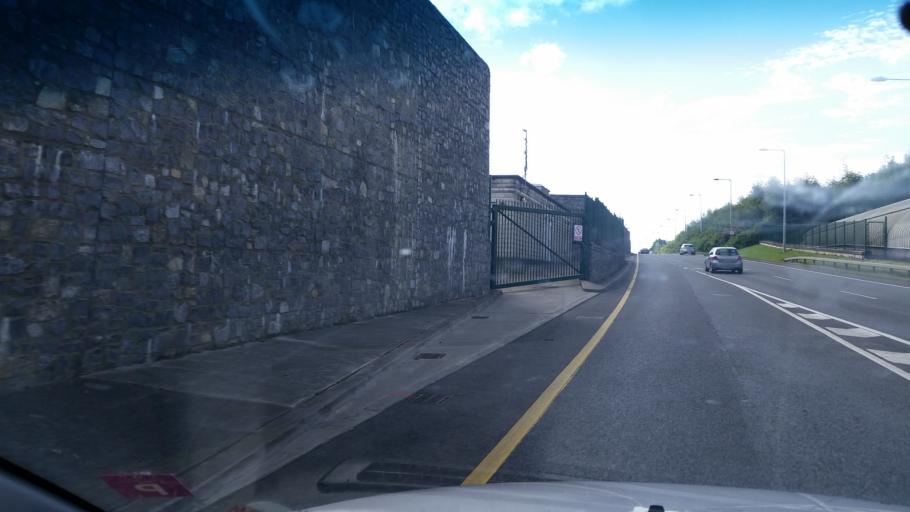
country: IE
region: Leinster
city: Beaumont
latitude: 53.3952
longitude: -6.2397
